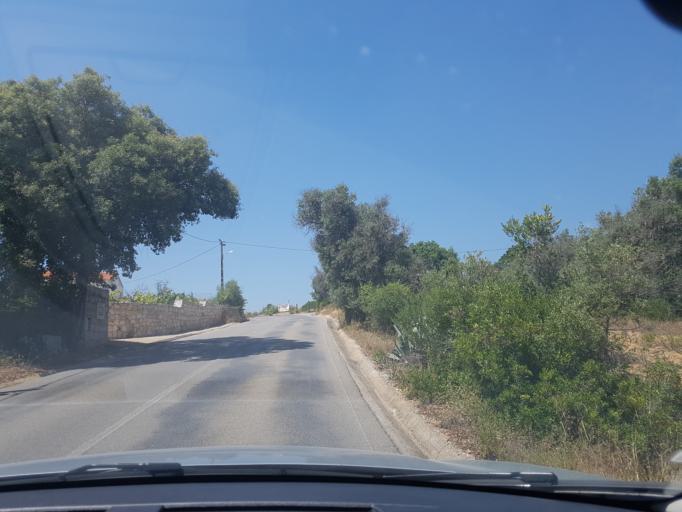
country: PT
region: Faro
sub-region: Lagoa
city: Carvoeiro
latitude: 37.1053
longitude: -8.4303
